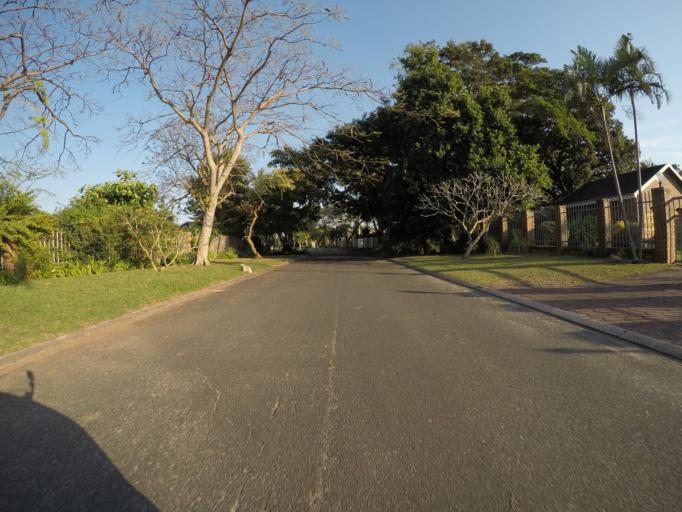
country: ZA
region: KwaZulu-Natal
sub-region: uThungulu District Municipality
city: Richards Bay
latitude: -28.7740
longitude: 32.1136
